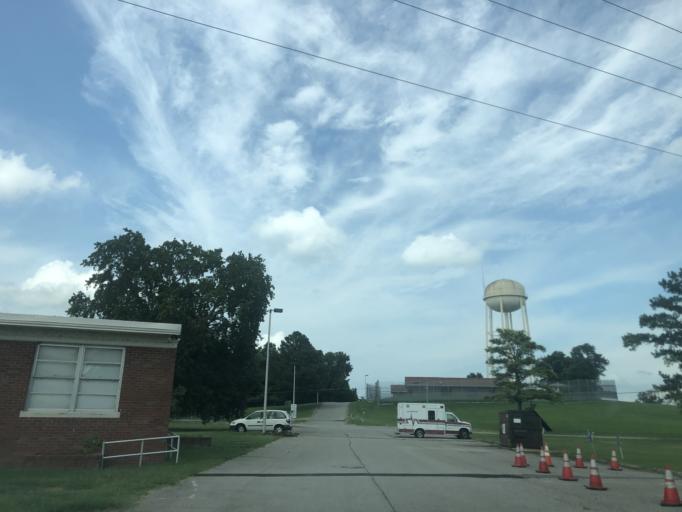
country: US
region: Tennessee
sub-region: Davidson County
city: Lakewood
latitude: 36.1634
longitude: -86.6445
